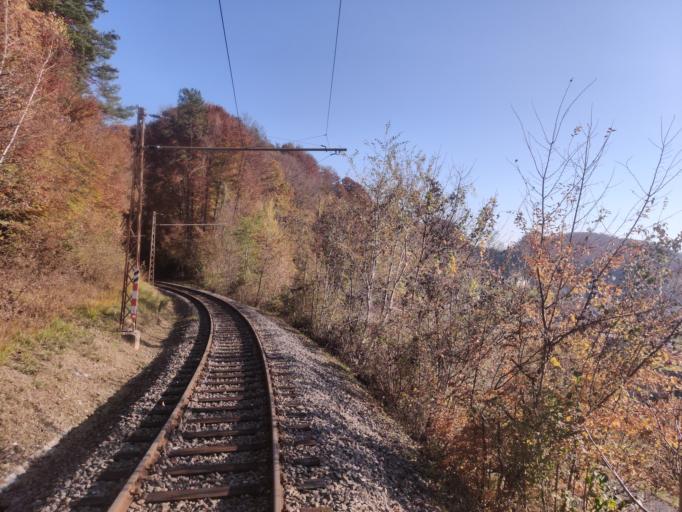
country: AT
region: Styria
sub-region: Politischer Bezirk Suedoststeiermark
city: Gnas
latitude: 46.8812
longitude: 15.8317
